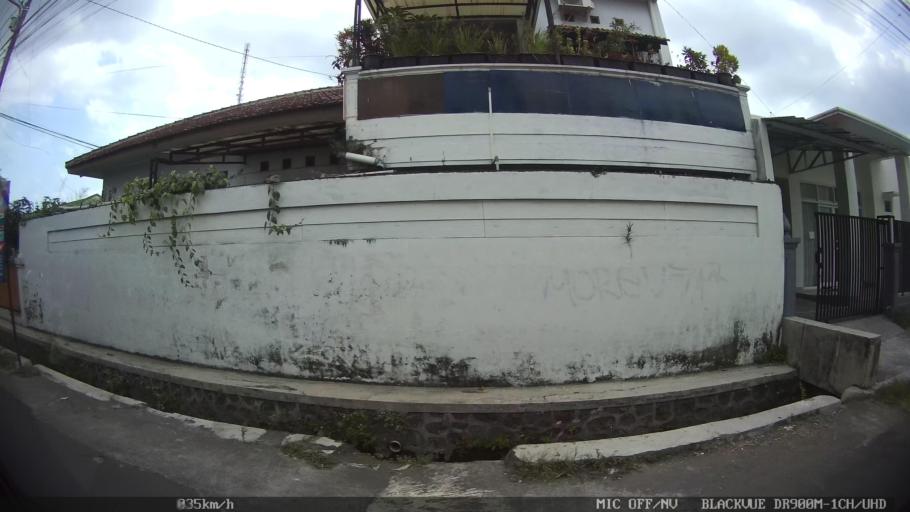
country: ID
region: Daerah Istimewa Yogyakarta
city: Yogyakarta
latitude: -7.7716
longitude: 110.3381
